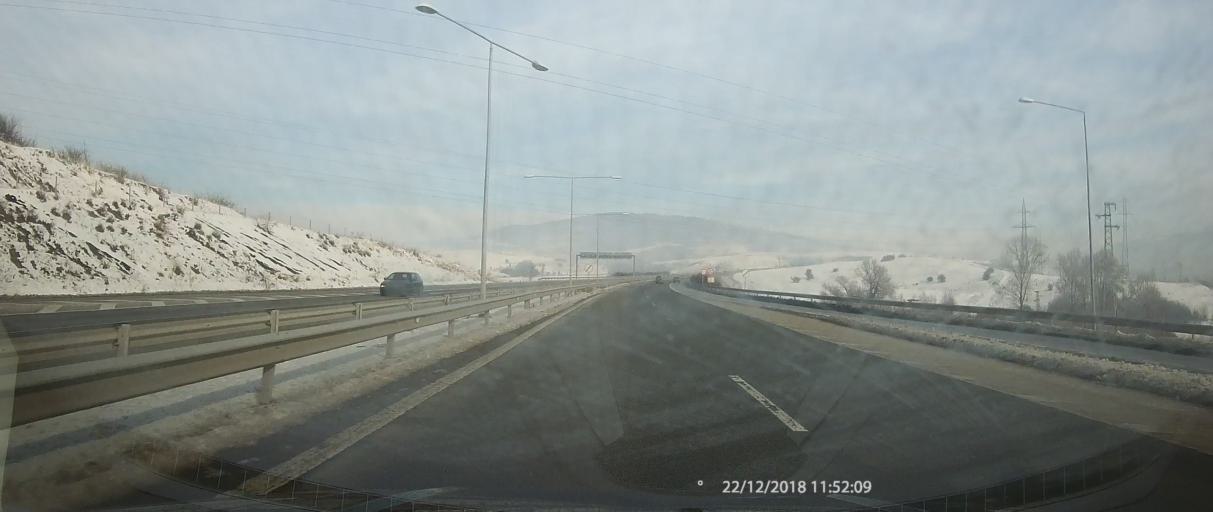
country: BG
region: Pernik
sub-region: Obshtina Pernik
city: Pernik
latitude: 42.6037
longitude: 23.1266
